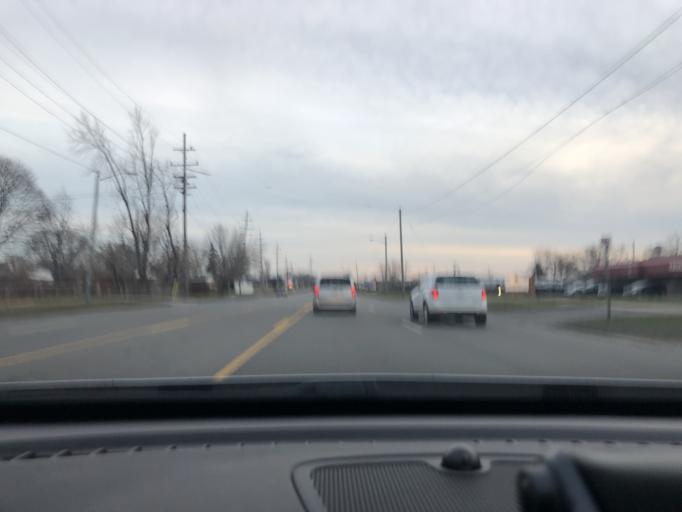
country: US
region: Michigan
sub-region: Wayne County
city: Allen Park
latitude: 42.2453
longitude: -83.2307
